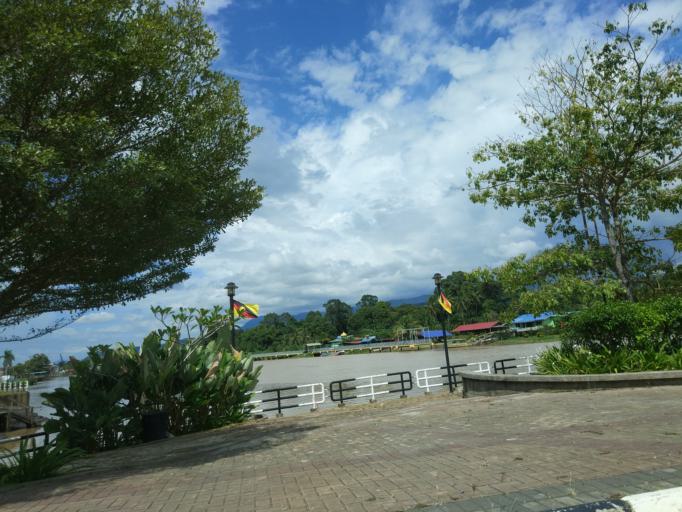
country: BN
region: Temburong
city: Bangar
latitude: 4.8582
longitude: 115.4079
